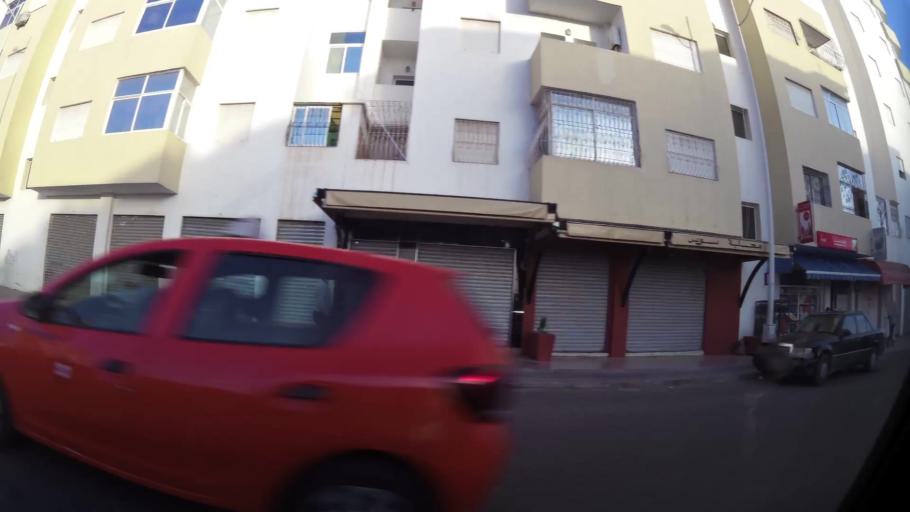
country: MA
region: Oued ed Dahab-Lagouira
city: Dakhla
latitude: 30.3992
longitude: -9.5561
